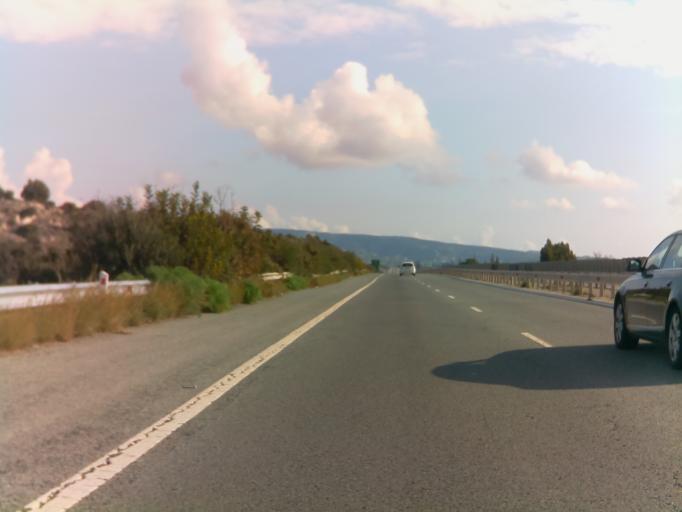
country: CY
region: Limassol
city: Pyrgos
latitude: 34.7461
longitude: 33.2941
